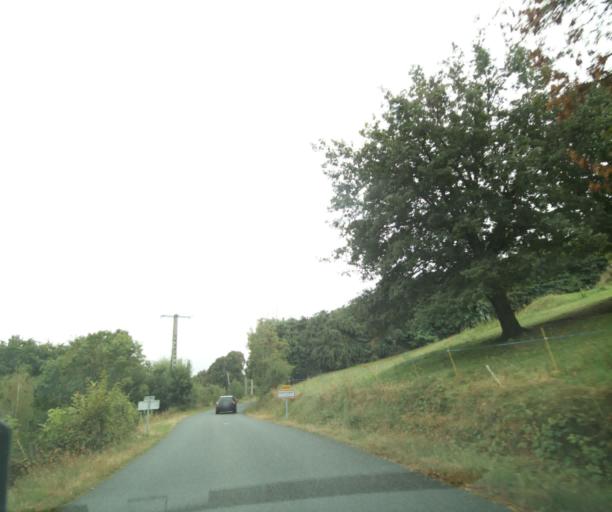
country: FR
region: Auvergne
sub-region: Departement du Puy-de-Dome
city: Durtol
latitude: 45.7986
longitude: 3.0302
